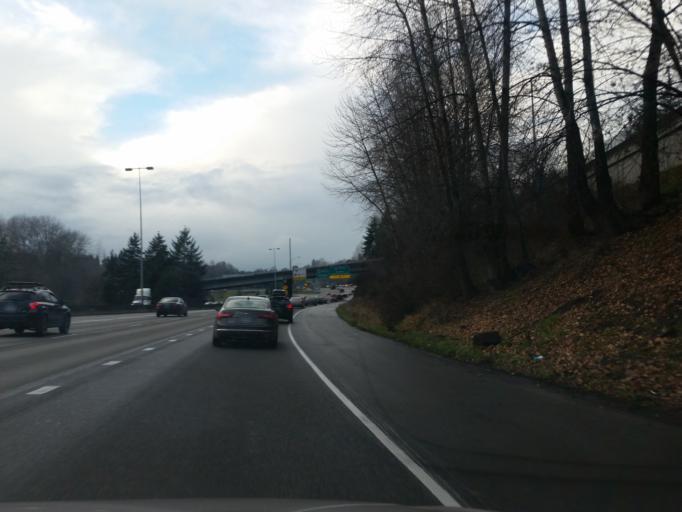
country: US
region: Washington
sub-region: King County
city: Tukwila
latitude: 47.4621
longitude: -122.2553
